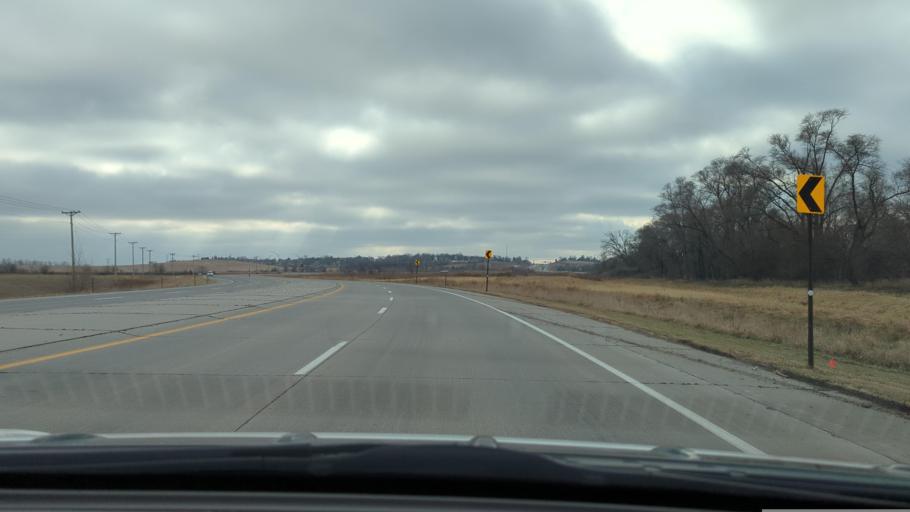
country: US
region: Nebraska
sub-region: Sarpy County
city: Offutt Air Force Base
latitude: 41.1081
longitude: -95.9283
